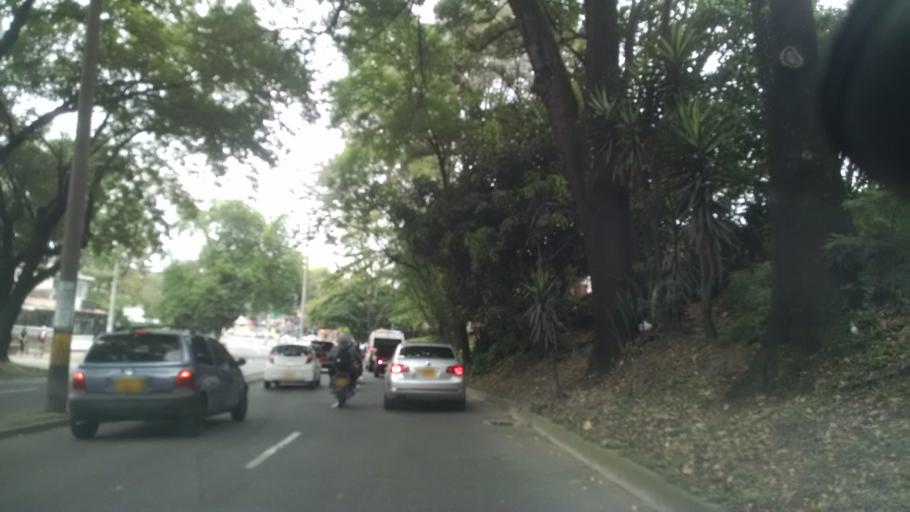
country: CO
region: Antioquia
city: Medellin
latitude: 6.2534
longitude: -75.5999
